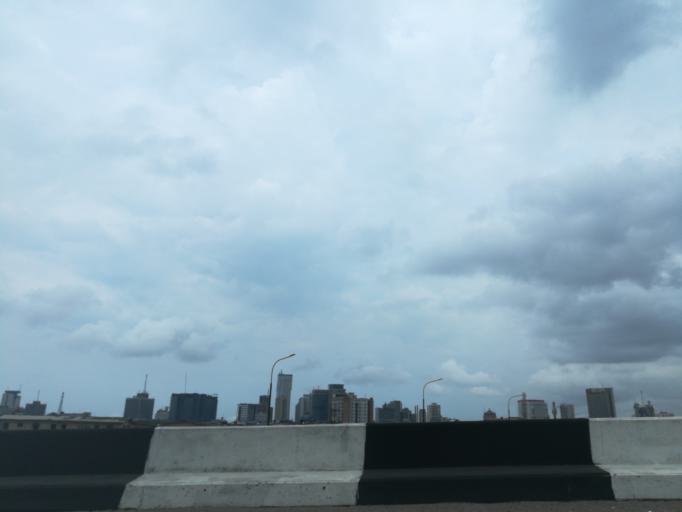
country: NG
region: Lagos
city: Lagos
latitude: 6.4599
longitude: 3.3959
